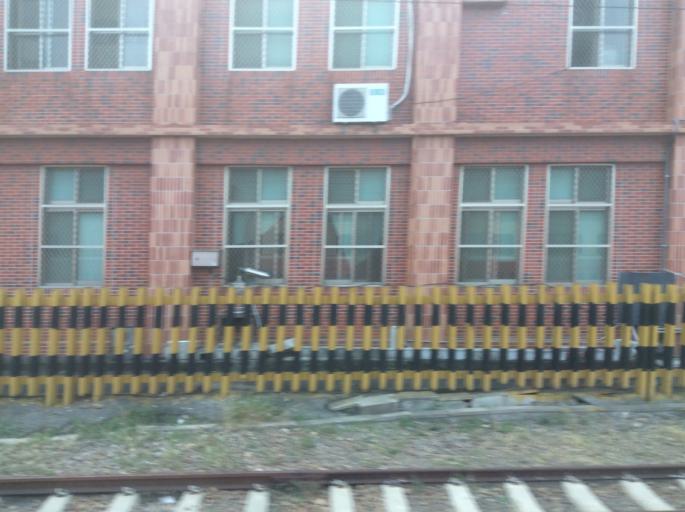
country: TW
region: Taiwan
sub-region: Nantou
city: Nantou
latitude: 23.8121
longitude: 120.6199
